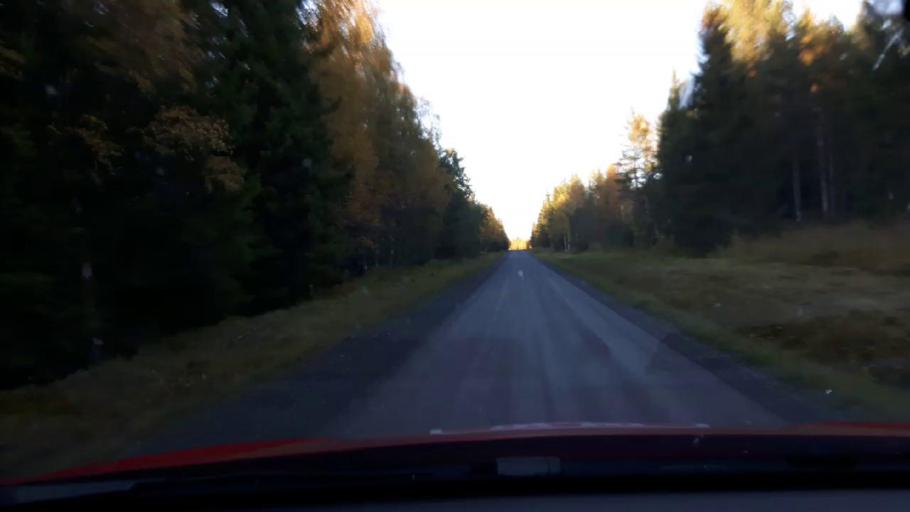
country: SE
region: Jaemtland
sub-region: Krokoms Kommun
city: Krokom
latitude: 63.4223
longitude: 14.6076
